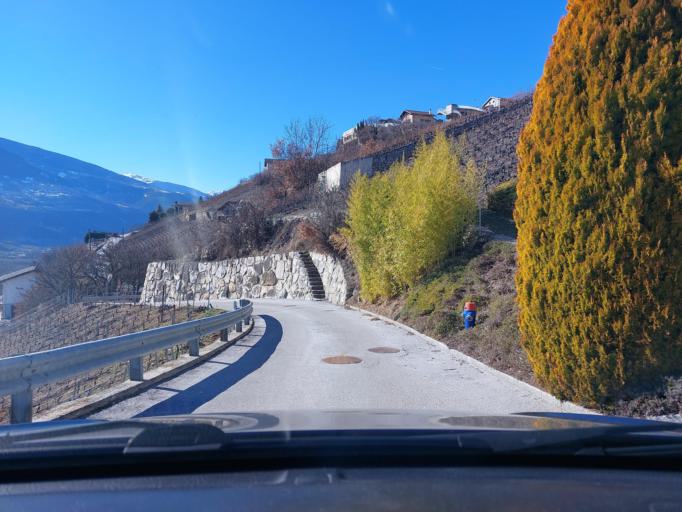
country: CH
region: Valais
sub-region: Sierre District
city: Chalais
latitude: 46.2852
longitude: 7.5066
